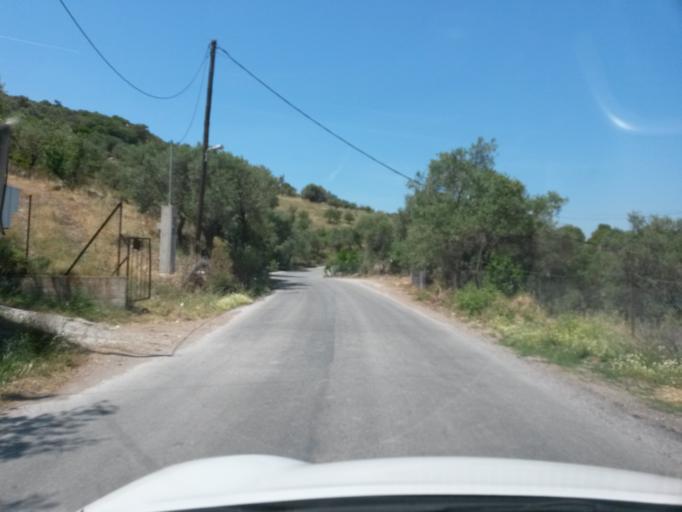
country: GR
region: North Aegean
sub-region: Nomos Lesvou
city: Pamfylla
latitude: 39.2397
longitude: 26.4365
